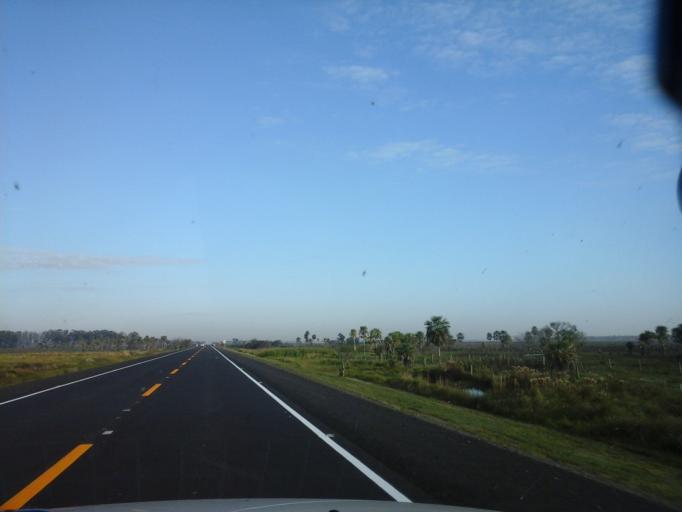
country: PY
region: Neembucu
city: Cerrito
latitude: -26.8675
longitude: -57.8111
